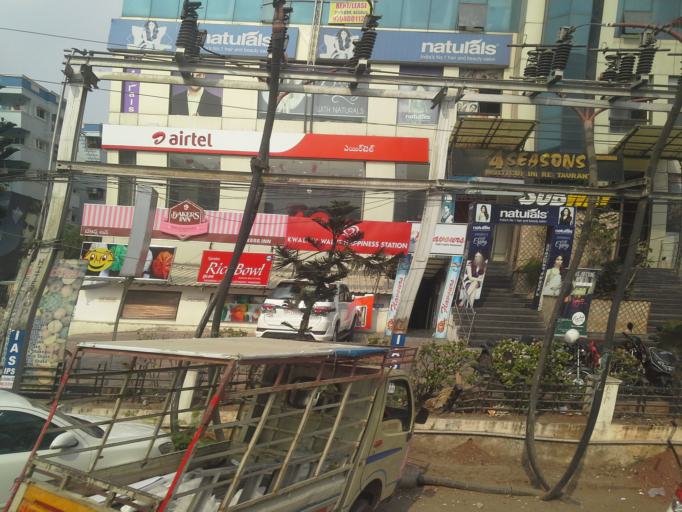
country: IN
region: Telangana
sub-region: Rangareddi
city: Kukatpalli
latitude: 17.4580
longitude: 78.3715
